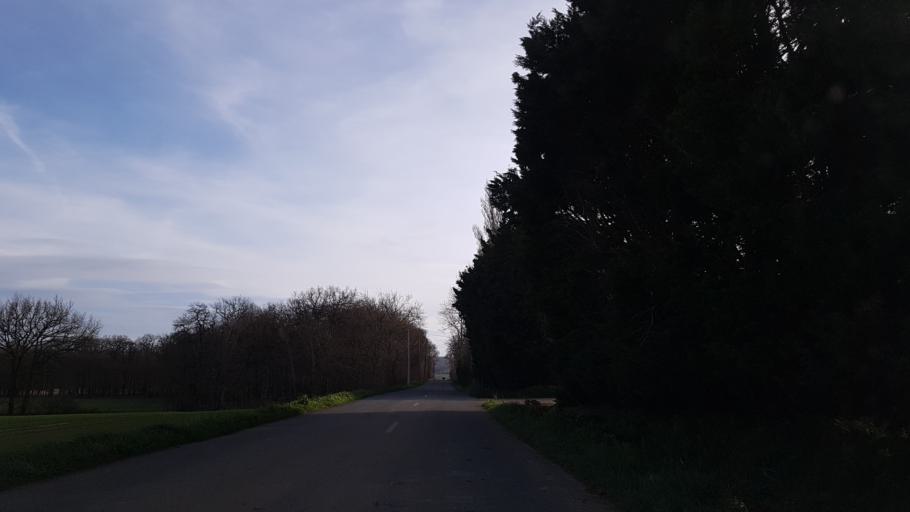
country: FR
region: Languedoc-Roussillon
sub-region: Departement de l'Aude
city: Villeneuve-la-Comptal
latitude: 43.1975
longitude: 1.9058
